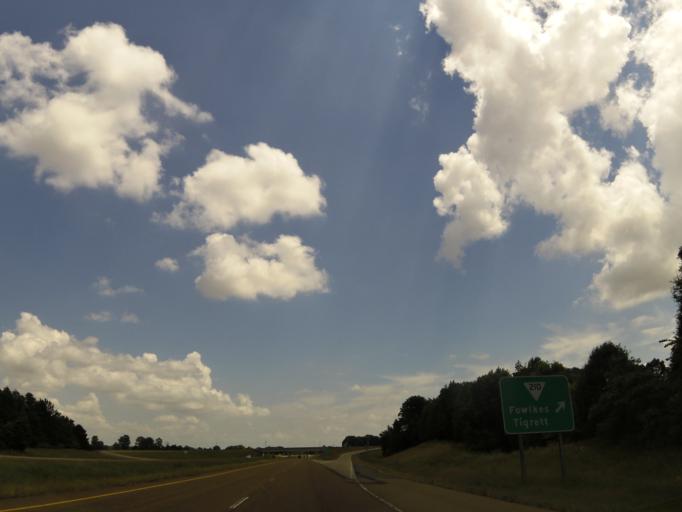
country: US
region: Tennessee
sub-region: Dyer County
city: Dyersburg
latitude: 35.9687
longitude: -89.3340
